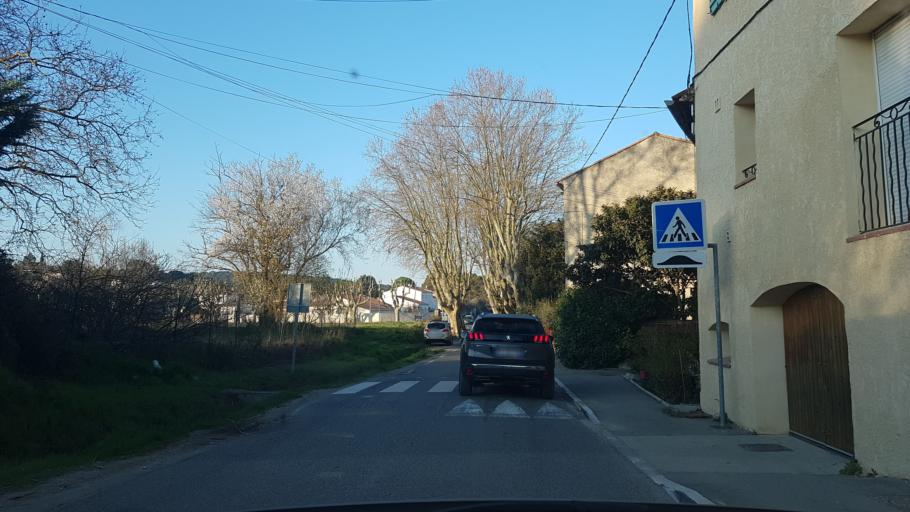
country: FR
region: Provence-Alpes-Cote d'Azur
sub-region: Departement des Bouches-du-Rhone
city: Cabries
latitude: 43.4475
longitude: 5.3805
